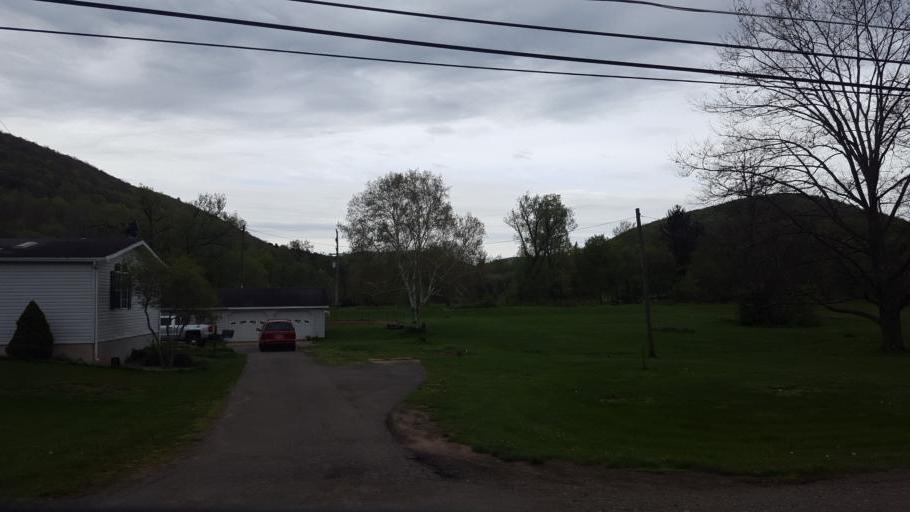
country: US
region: Pennsylvania
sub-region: Tioga County
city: Westfield
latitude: 41.9133
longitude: -77.6014
